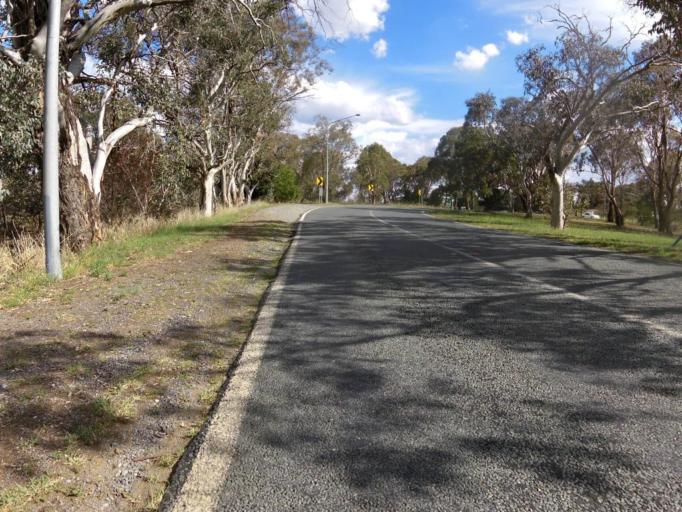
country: AU
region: Australian Capital Territory
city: Belconnen
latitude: -35.1800
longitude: 149.0736
